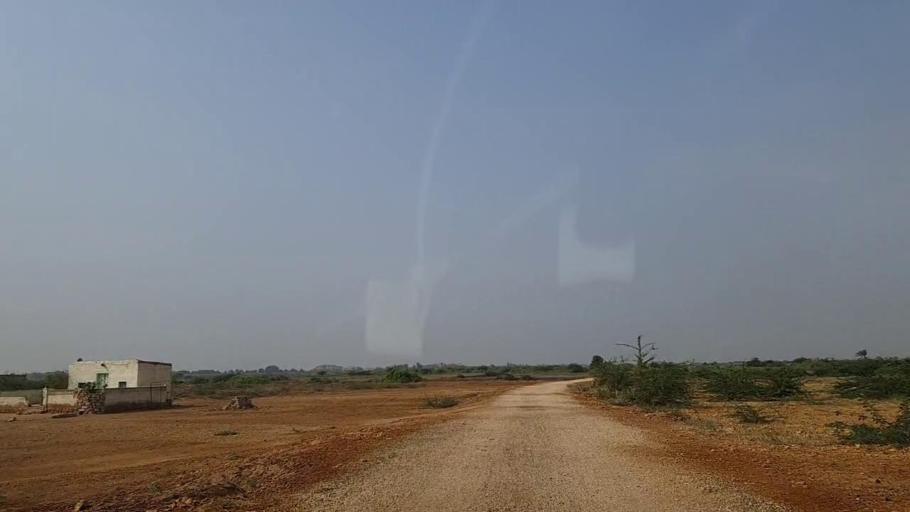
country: PK
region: Sindh
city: Thatta
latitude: 24.7204
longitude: 67.8251
